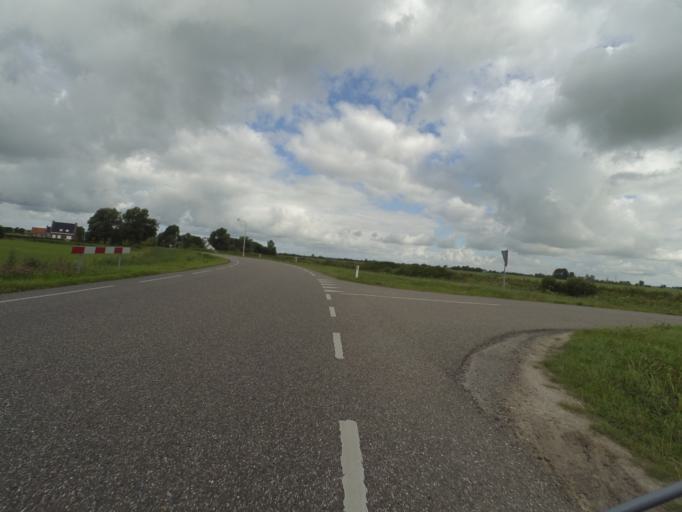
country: NL
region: Friesland
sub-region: Gemeente Kollumerland en Nieuwkruisland
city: Kollum
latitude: 53.2630
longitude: 6.1677
